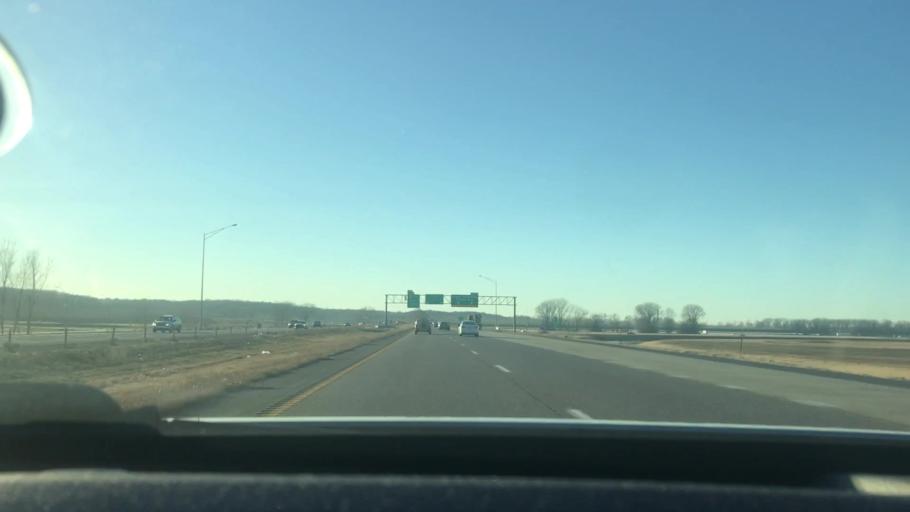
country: US
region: Missouri
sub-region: Platte County
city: Riverside
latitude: 39.1609
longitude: -94.6338
